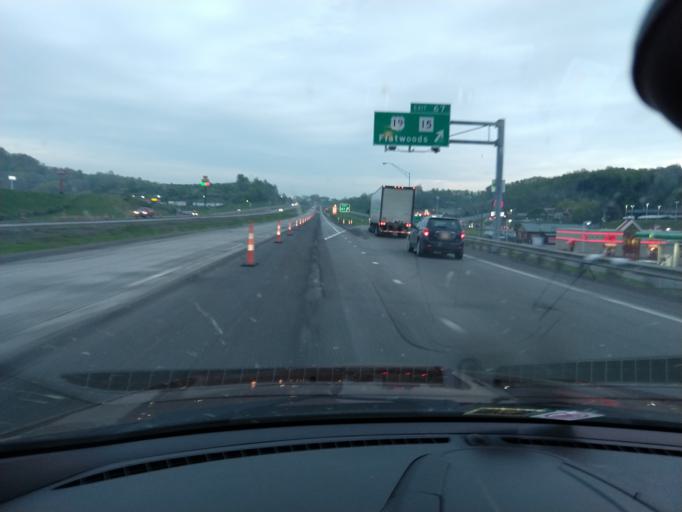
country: US
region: West Virginia
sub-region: Braxton County
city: Sutton
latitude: 38.7005
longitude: -80.6653
